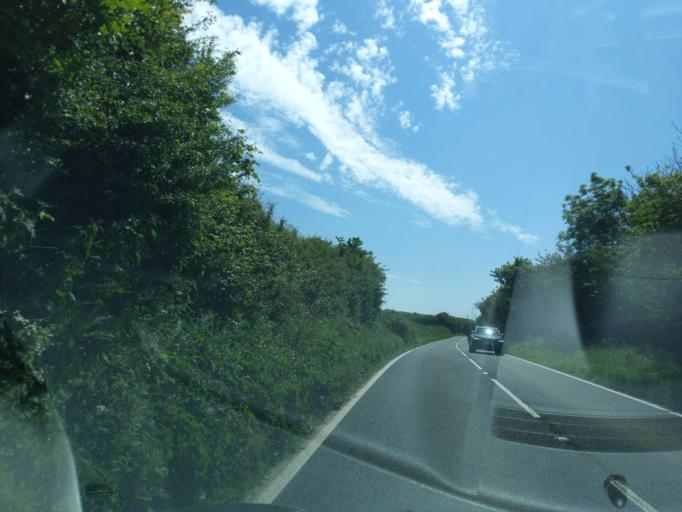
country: GB
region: England
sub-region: Cornwall
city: Camelford
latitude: 50.6066
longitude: -4.6916
